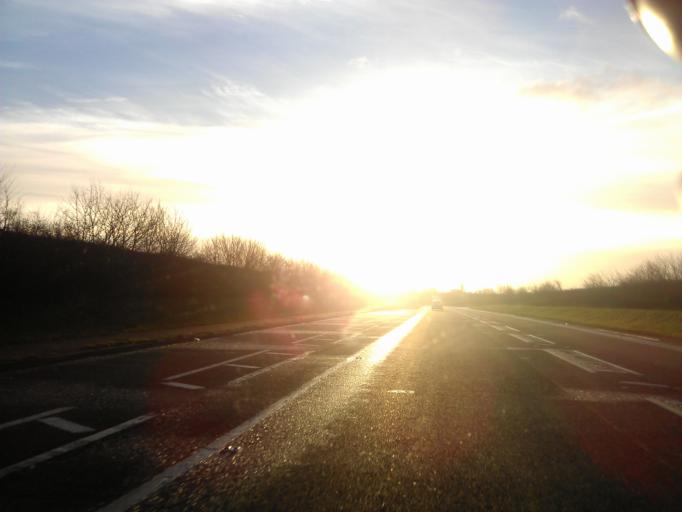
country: GB
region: England
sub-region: Essex
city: Little Clacton
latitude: 51.8142
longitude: 1.1419
